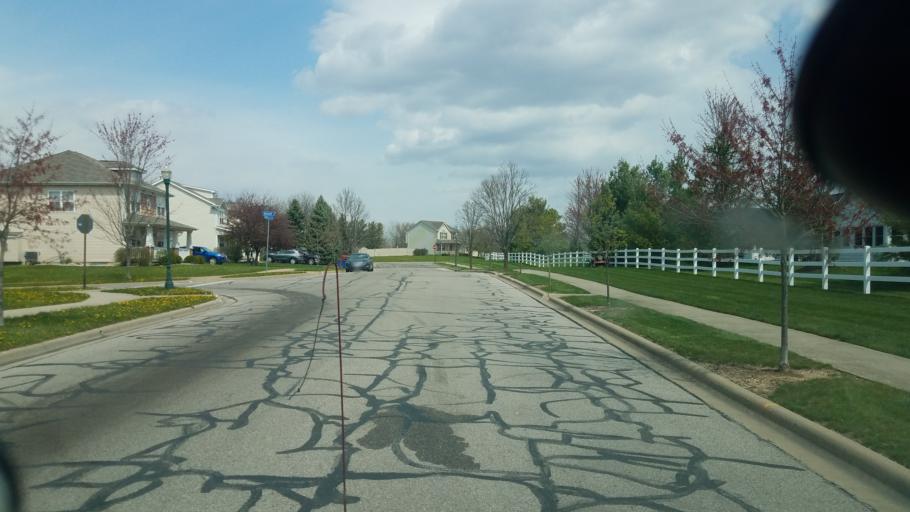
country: US
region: Ohio
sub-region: Delaware County
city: Delaware
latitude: 40.3073
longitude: -83.1151
